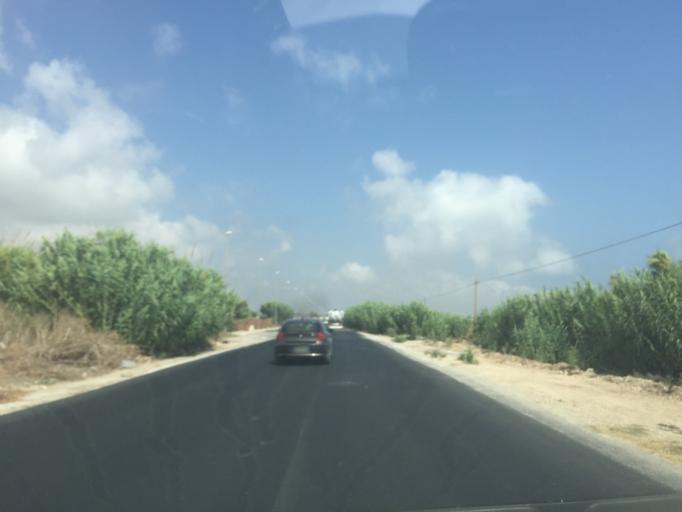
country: IT
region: Sicily
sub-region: Ragusa
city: Marina di Ragusa
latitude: 36.7806
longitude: 14.5719
